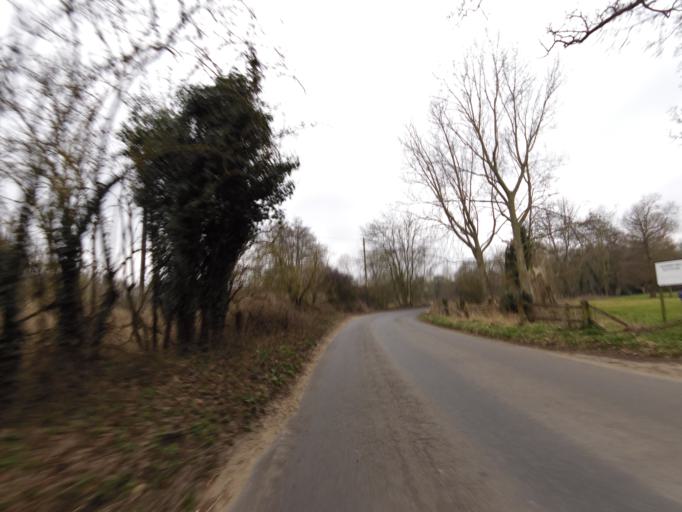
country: GB
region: England
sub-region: Suffolk
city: Wickham Market
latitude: 52.1609
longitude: 1.3566
